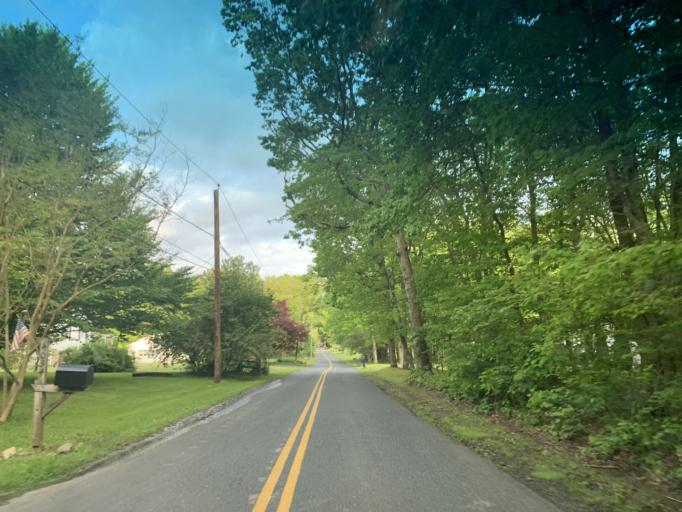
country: US
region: Pennsylvania
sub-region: York County
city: Susquehanna Trails
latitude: 39.6769
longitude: -76.2440
